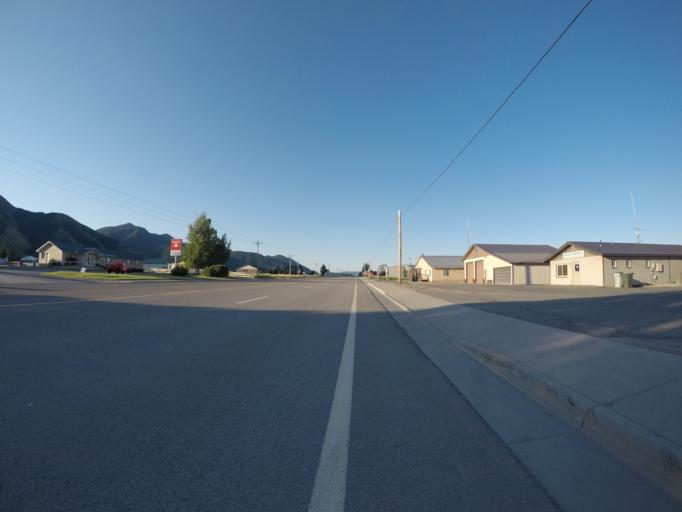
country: US
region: Wyoming
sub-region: Lincoln County
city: Afton
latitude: 42.7470
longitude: -110.9335
